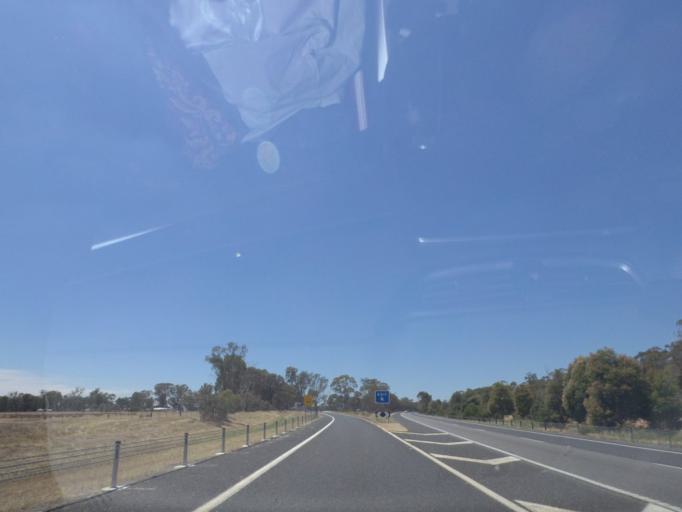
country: AU
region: Victoria
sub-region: Benalla
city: Benalla
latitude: -36.5759
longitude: 145.9272
